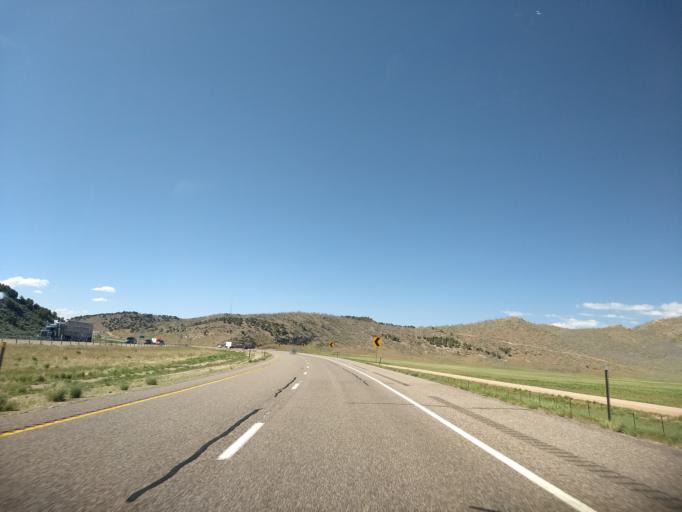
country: US
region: Utah
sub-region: Beaver County
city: Beaver
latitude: 38.6699
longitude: -112.5882
